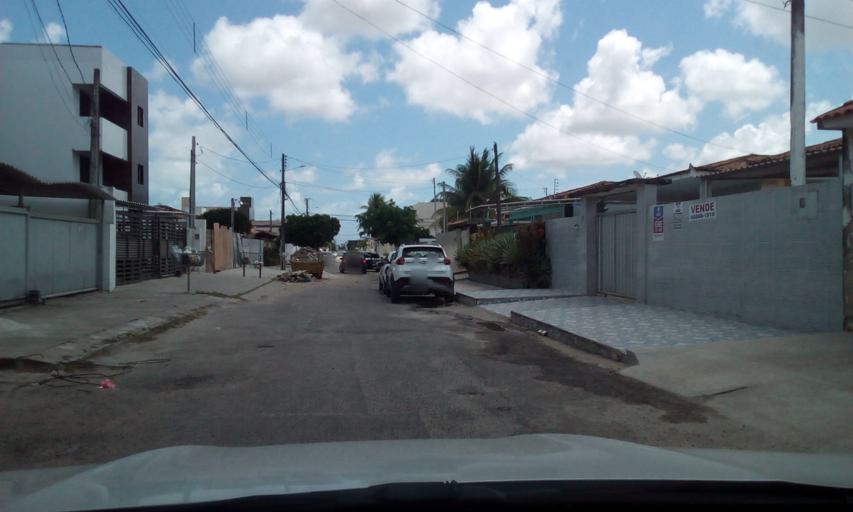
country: BR
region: Paraiba
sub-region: Joao Pessoa
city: Joao Pessoa
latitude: -7.1728
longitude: -34.8598
